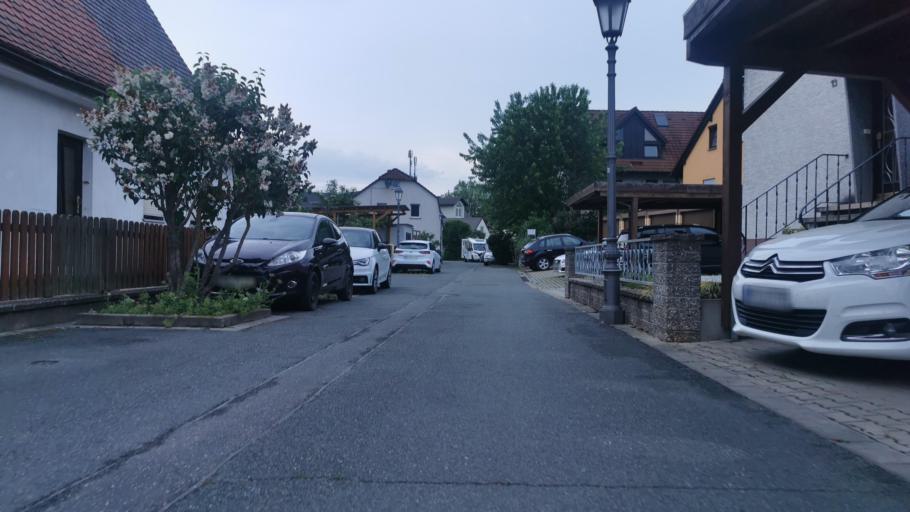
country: DE
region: Bavaria
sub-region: Regierungsbezirk Mittelfranken
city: Hochstadt an der Aisch
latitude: 49.7022
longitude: 10.8091
